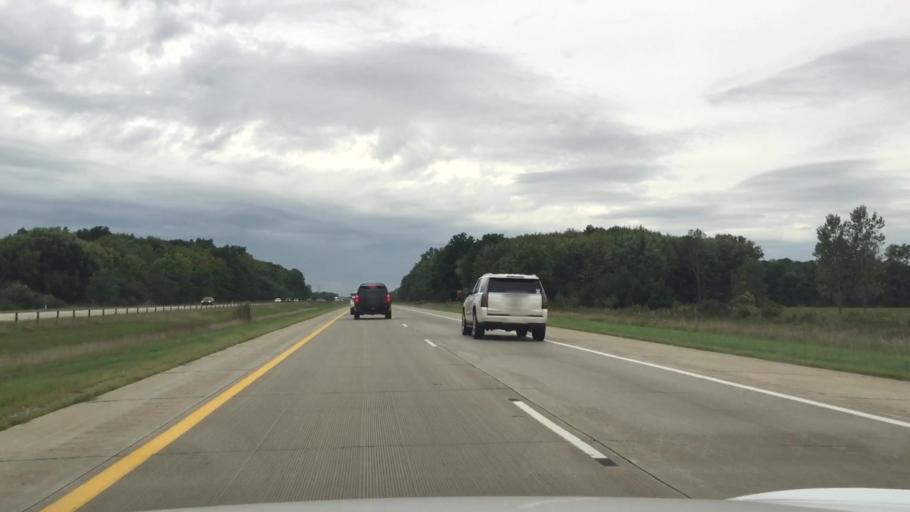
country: US
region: Michigan
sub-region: Macomb County
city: Richmond
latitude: 42.7635
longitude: -82.6940
